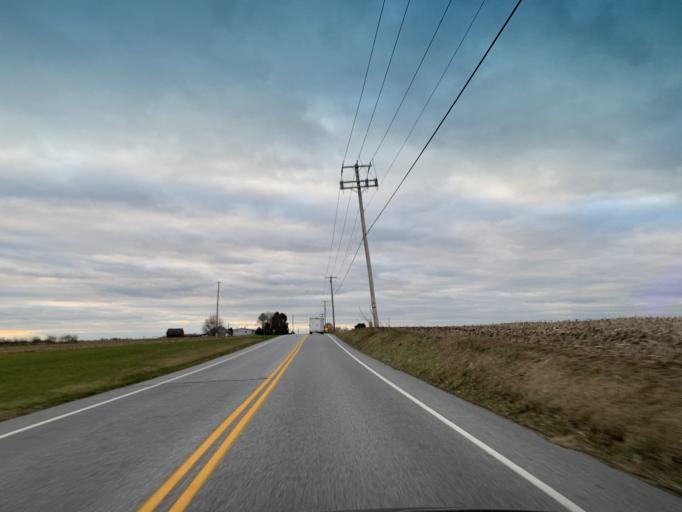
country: US
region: Pennsylvania
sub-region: York County
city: Shrewsbury
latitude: 39.7822
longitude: -76.6351
